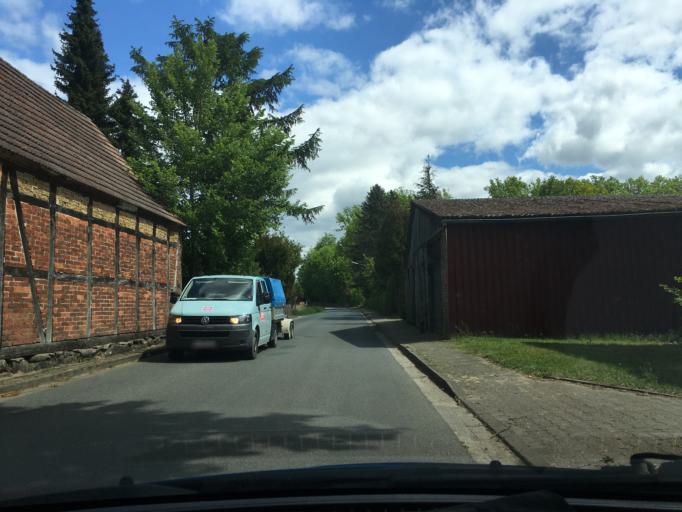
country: DE
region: Lower Saxony
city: Suderburg
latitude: 52.9294
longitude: 10.4440
